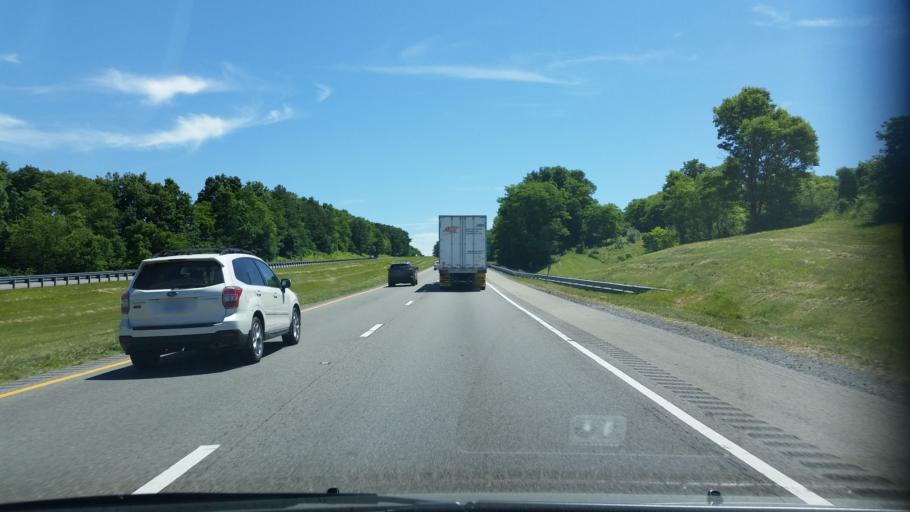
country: US
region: Virginia
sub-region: Wythe County
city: Rural Retreat
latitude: 36.9100
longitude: -81.2959
